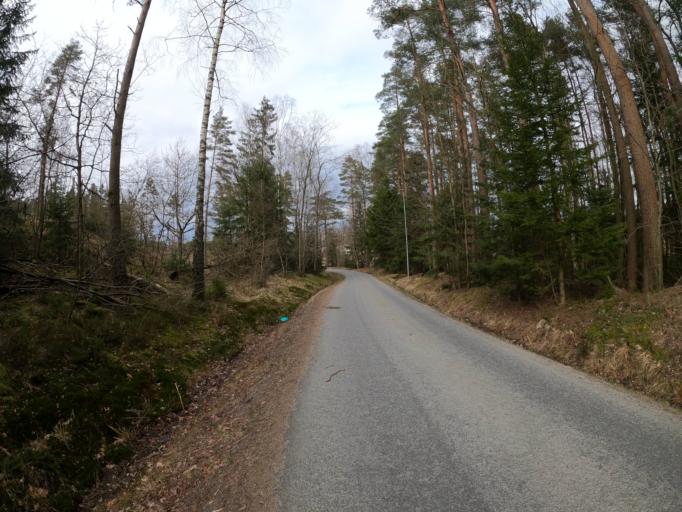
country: SE
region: Vaestra Goetaland
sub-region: Molndal
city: Kallered
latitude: 57.6193
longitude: 12.0818
